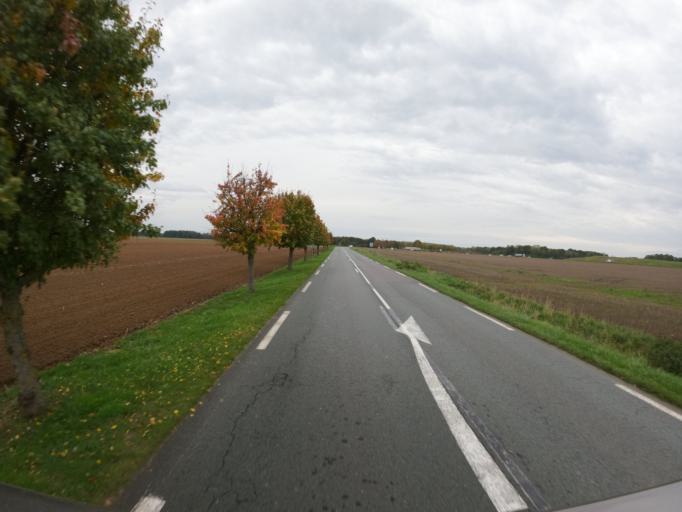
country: FR
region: Ile-de-France
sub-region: Departement de Seine-et-Marne
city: Villeneuve-le-Comte
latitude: 48.8168
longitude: 2.8229
